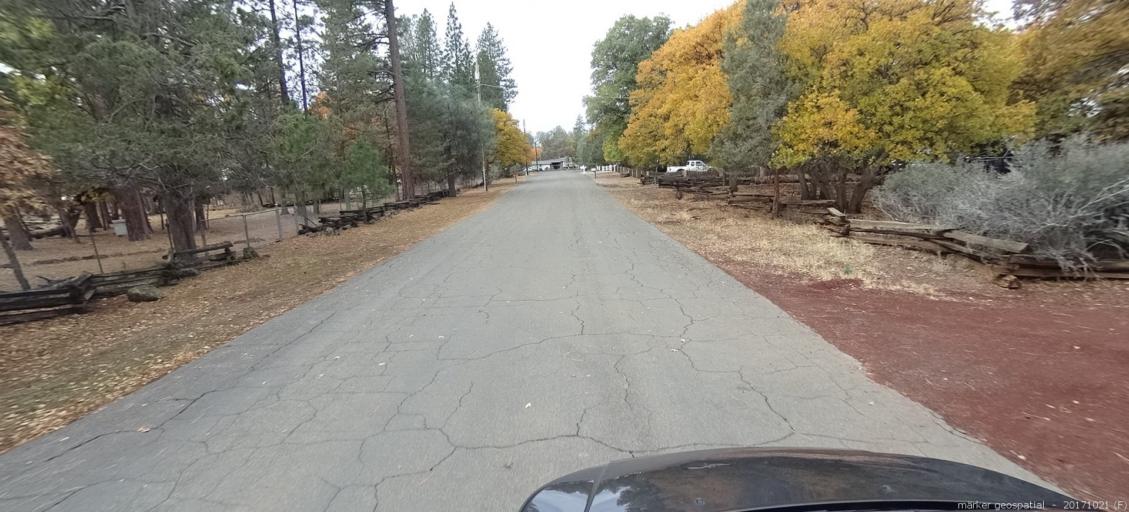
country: US
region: California
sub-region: Shasta County
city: Burney
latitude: 40.9168
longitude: -121.5556
